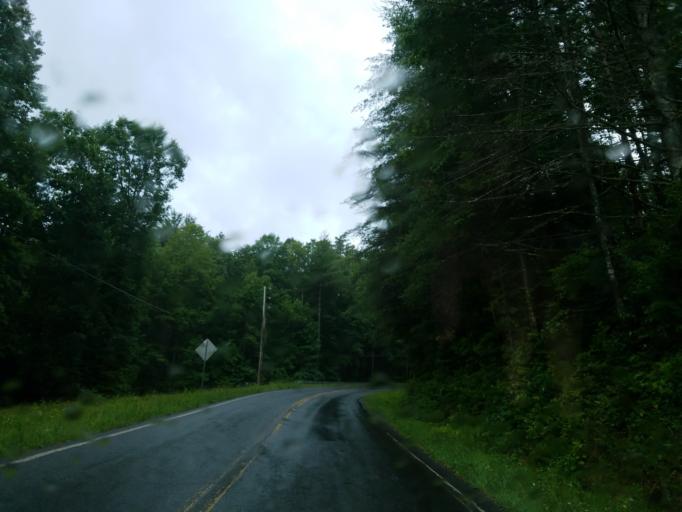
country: US
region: Georgia
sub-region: Fannin County
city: Blue Ridge
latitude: 34.7721
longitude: -84.2553
